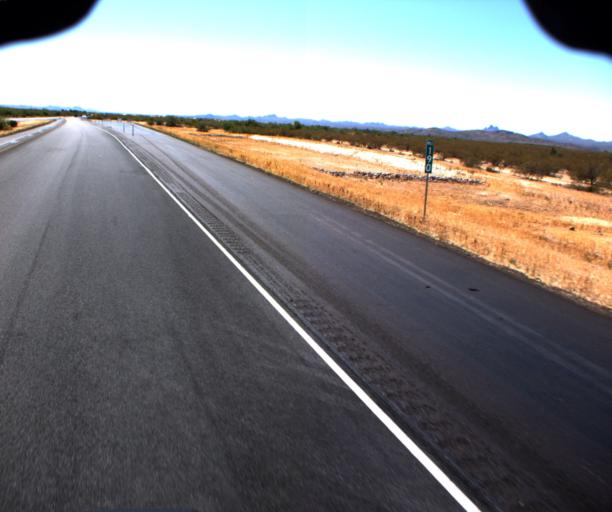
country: US
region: Arizona
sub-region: Yavapai County
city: Congress
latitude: 34.0573
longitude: -112.8561
